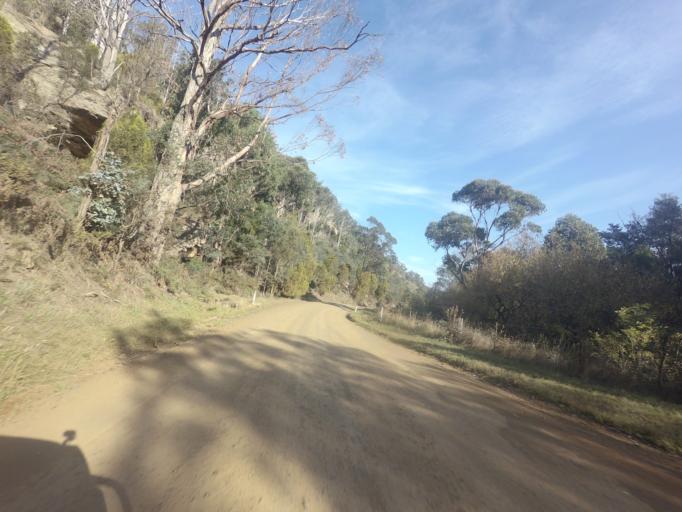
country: AU
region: Tasmania
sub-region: Sorell
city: Sorell
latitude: -42.4951
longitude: 147.4335
